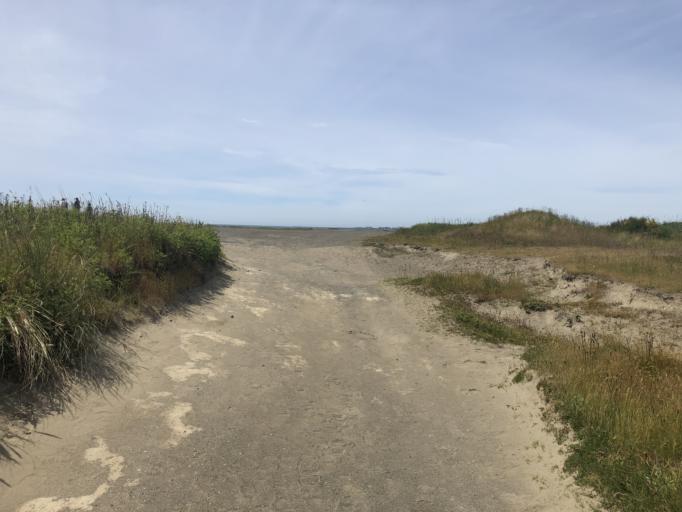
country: US
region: Washington
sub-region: Grays Harbor County
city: Westport
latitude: 46.9036
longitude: -124.1315
